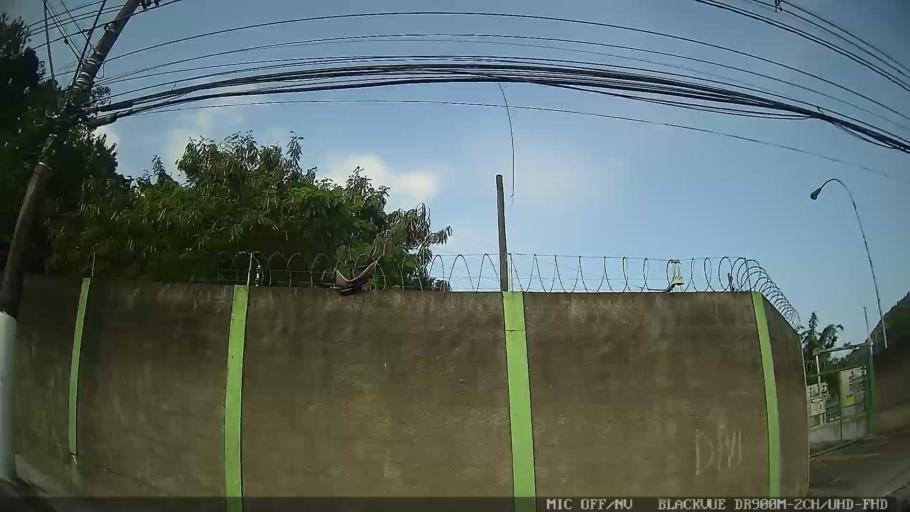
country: BR
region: Sao Paulo
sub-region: Guaruja
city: Guaruja
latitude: -23.9851
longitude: -46.2645
